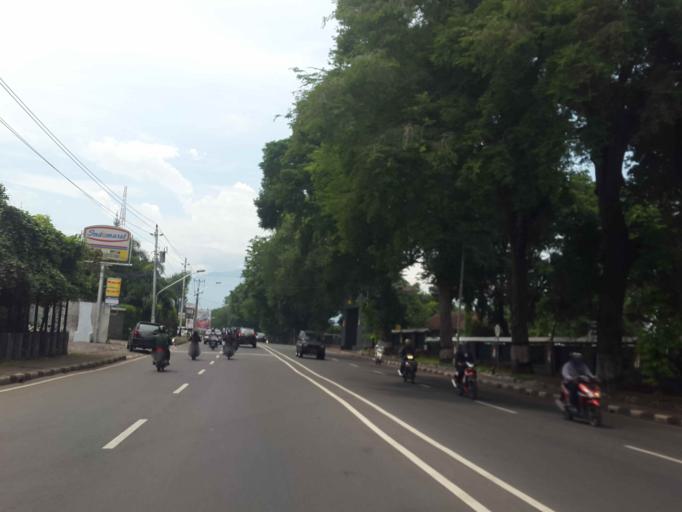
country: ID
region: Central Java
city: Semarang
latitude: -7.0537
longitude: 110.4163
